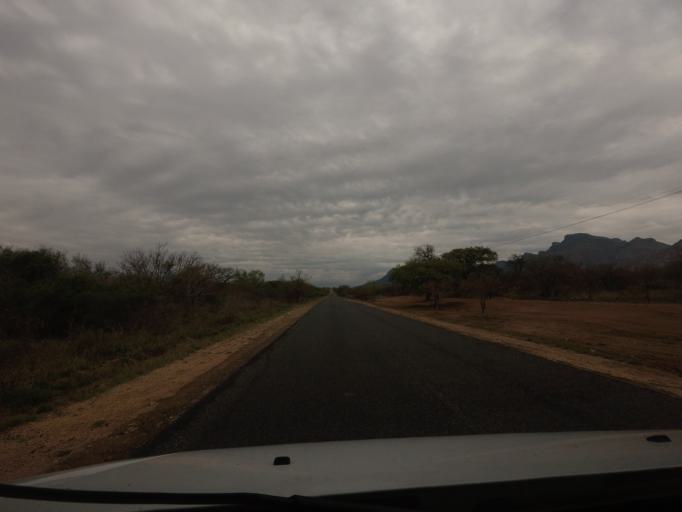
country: ZA
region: Limpopo
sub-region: Mopani District Municipality
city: Hoedspruit
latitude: -24.4706
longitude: 30.8777
